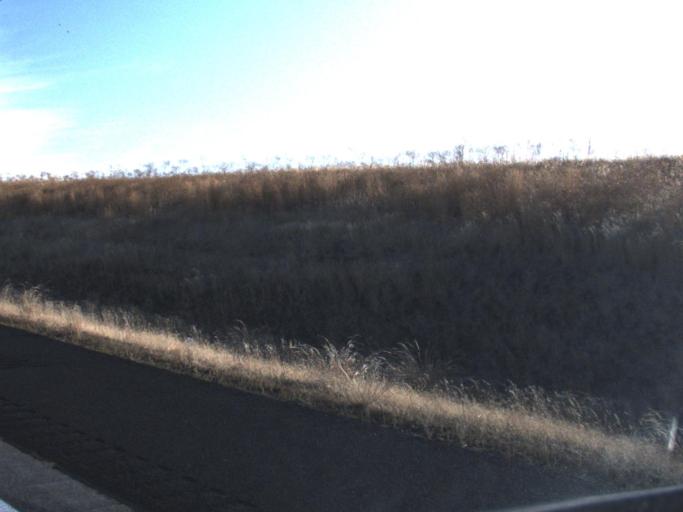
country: US
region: Washington
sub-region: Franklin County
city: Connell
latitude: 46.5899
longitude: -118.9609
